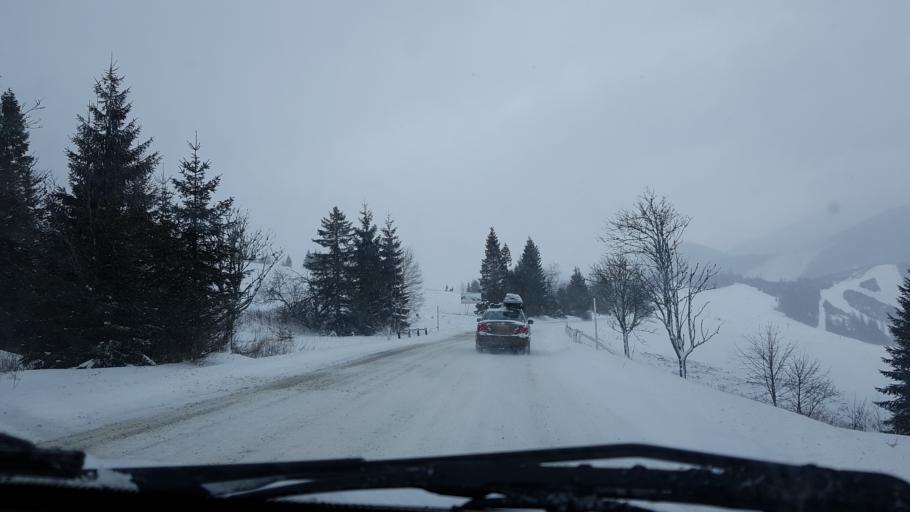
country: SK
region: Presovsky
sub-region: Okres Poprad
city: Zdiar
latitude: 49.2778
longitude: 20.2193
